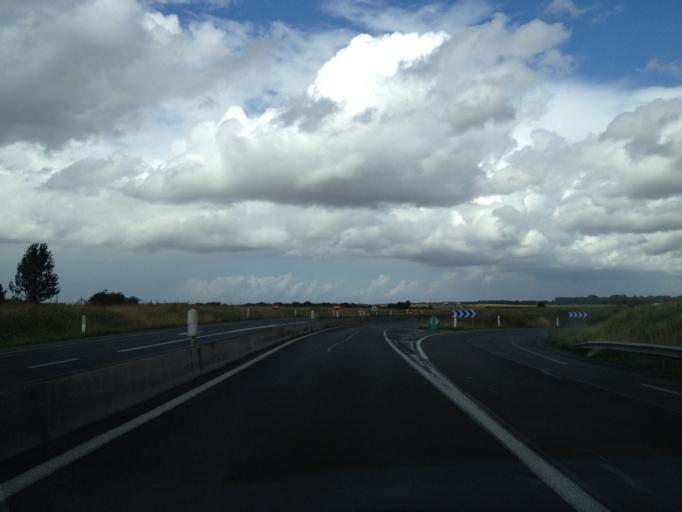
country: FR
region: Picardie
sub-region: Departement de la Somme
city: Abbeville
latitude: 50.1372
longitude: 1.8085
